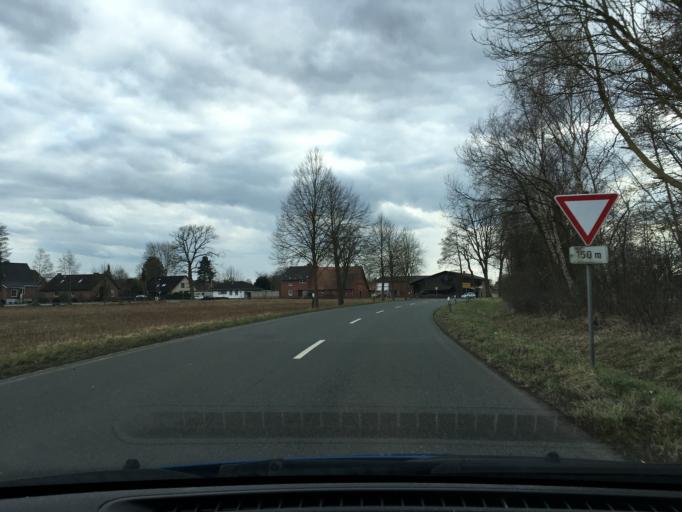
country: DE
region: Lower Saxony
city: Radbruch
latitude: 53.3134
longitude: 10.2793
